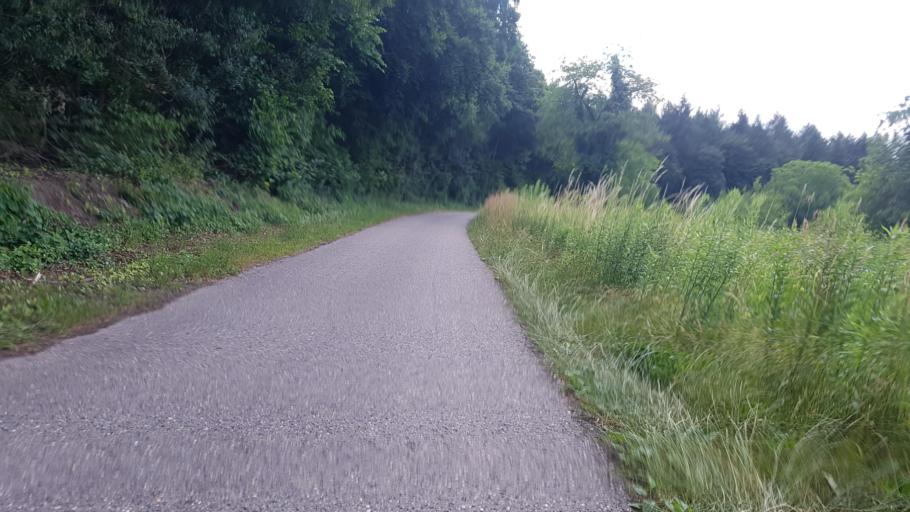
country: DE
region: Baden-Wuerttemberg
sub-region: Karlsruhe Region
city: Ubstadt-Weiher
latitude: 49.1658
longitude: 8.6706
